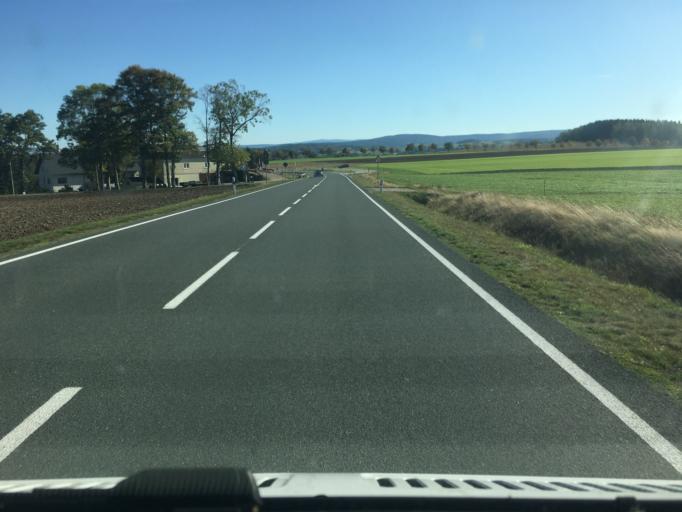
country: DE
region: Saxony
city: Schneeberg
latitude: 50.6034
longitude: 12.6086
